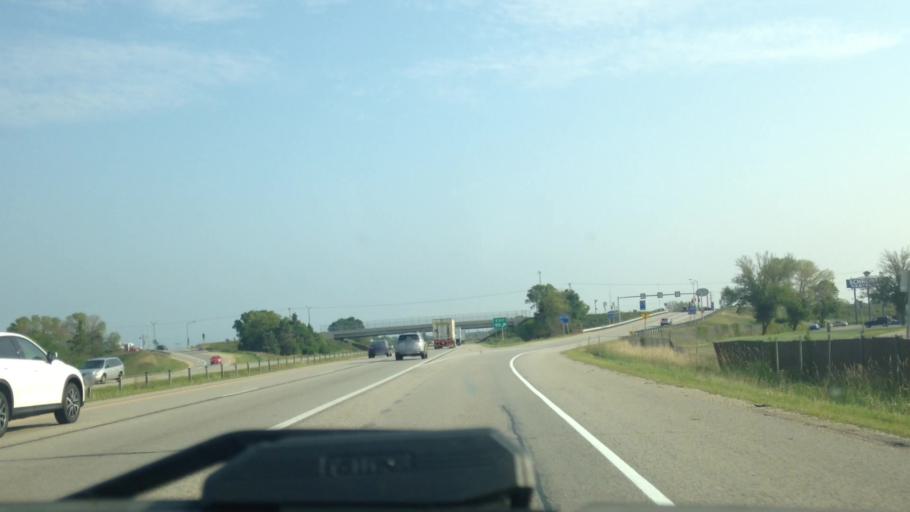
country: US
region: Wisconsin
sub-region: Fond du Lac County
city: North Fond du Lac
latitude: 43.7814
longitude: -88.4823
